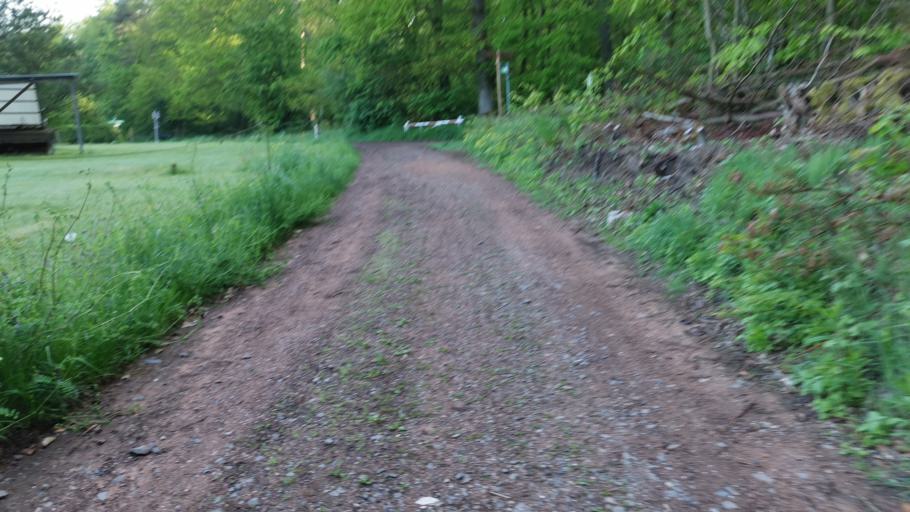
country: DE
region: Saarland
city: Sankt Ingbert
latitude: 49.2671
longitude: 7.1738
